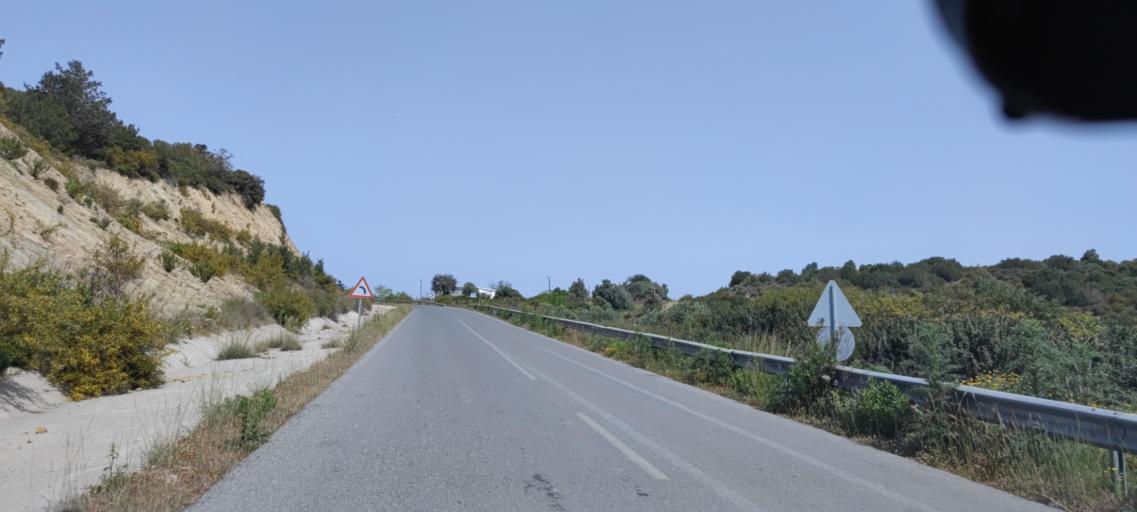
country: CY
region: Ammochostos
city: Rizokarpaso
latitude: 35.5894
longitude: 34.3923
